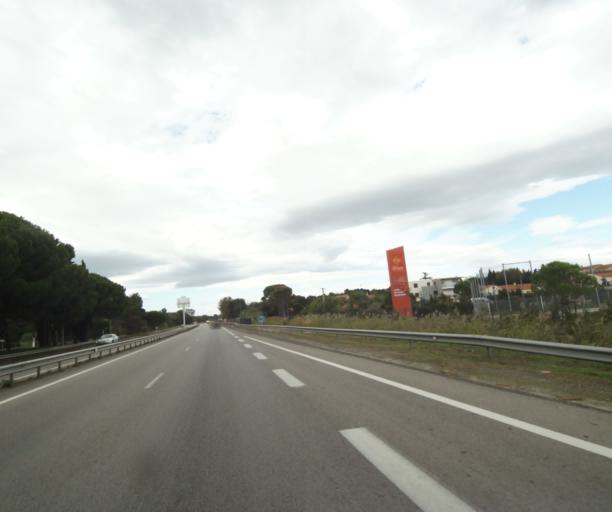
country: FR
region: Languedoc-Roussillon
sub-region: Departement des Pyrenees-Orientales
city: Argelers
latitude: 42.5665
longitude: 3.0030
